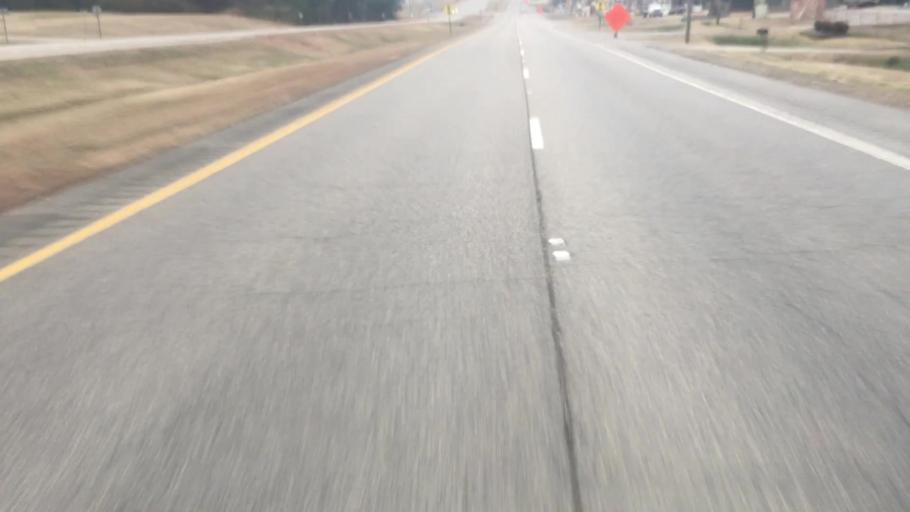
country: US
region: Alabama
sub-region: Walker County
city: Sumiton
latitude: 33.7606
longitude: -87.0670
